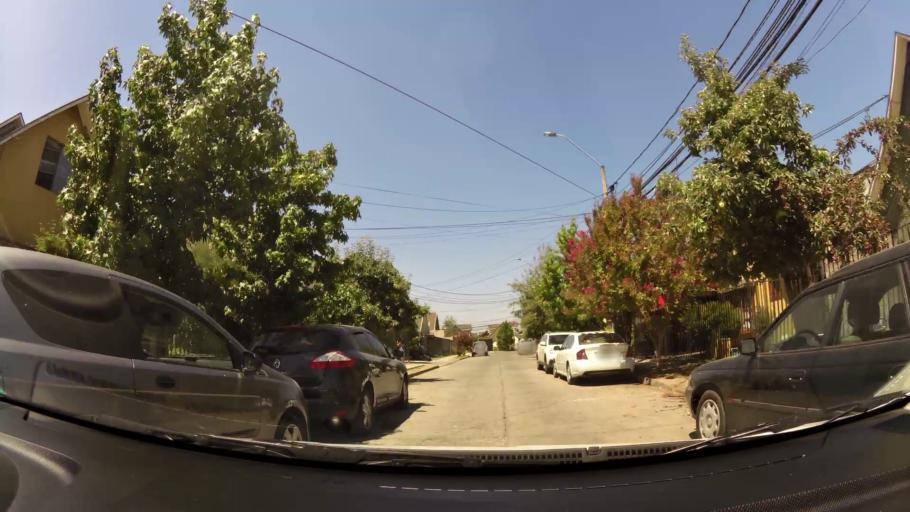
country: CL
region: Maule
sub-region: Provincia de Talca
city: Talca
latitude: -35.4257
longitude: -71.6199
